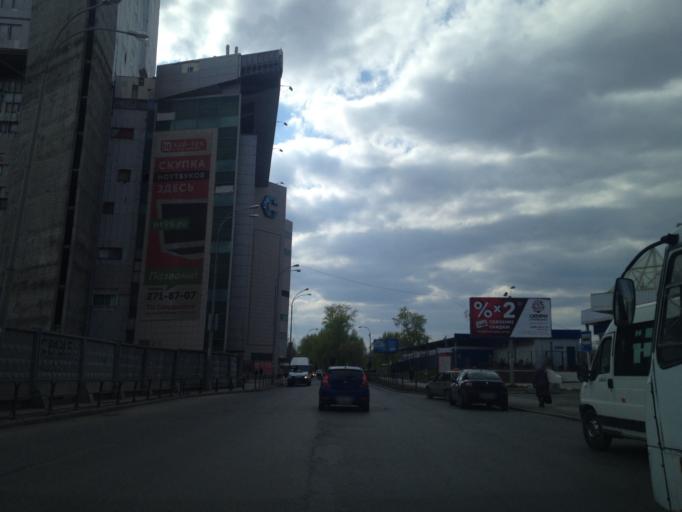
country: RU
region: Sverdlovsk
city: Yekaterinburg
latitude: 56.8572
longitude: 60.6001
